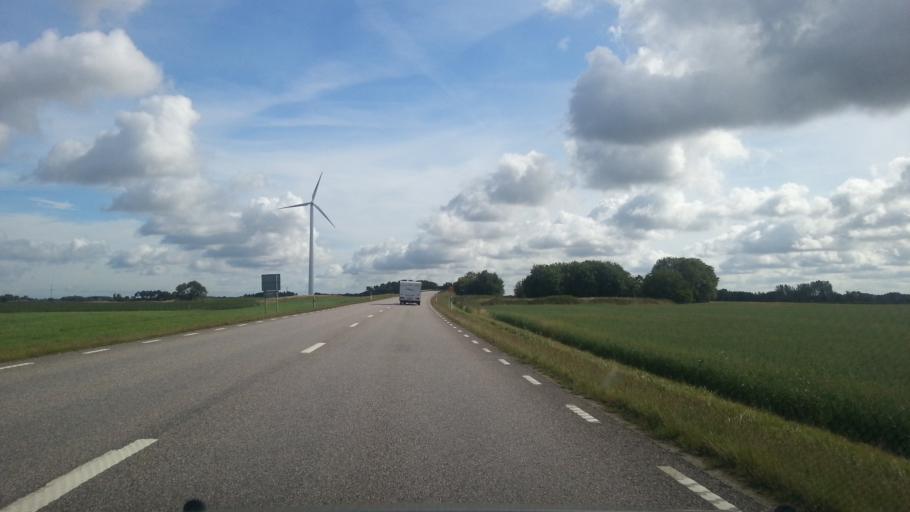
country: SE
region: Vaestra Goetaland
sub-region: Grastorps Kommun
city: Graestorp
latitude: 58.3396
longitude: 12.6217
